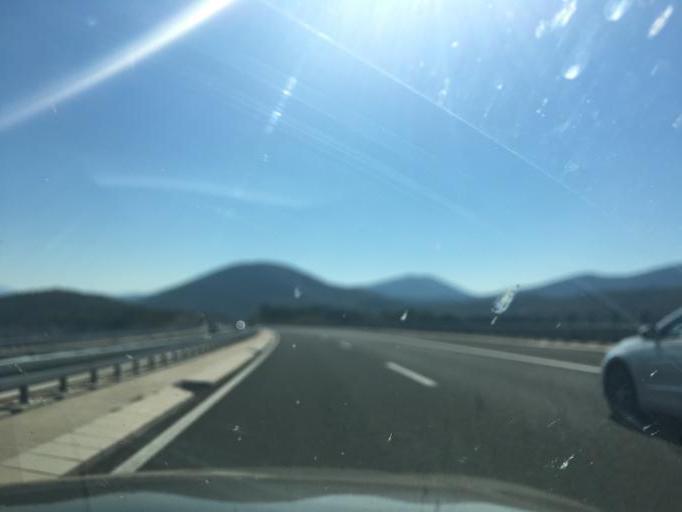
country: HR
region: Splitsko-Dalmatinska
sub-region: Grad Trogir
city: Trogir
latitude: 43.6454
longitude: 16.2014
